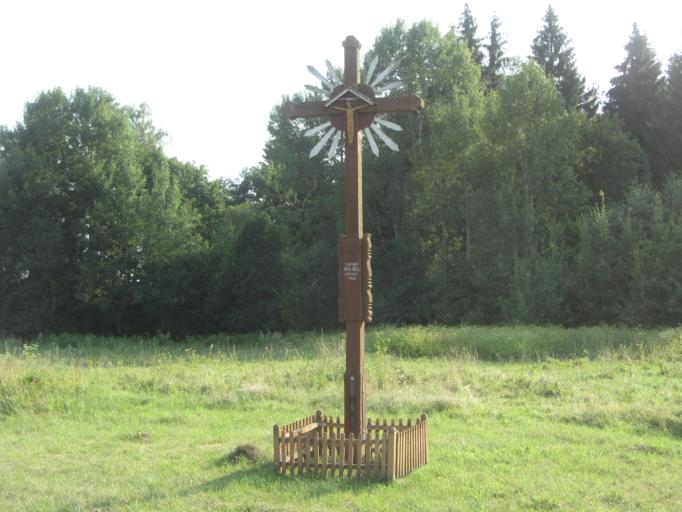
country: LT
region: Vilnius County
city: Ukmerge
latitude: 55.1314
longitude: 24.5972
